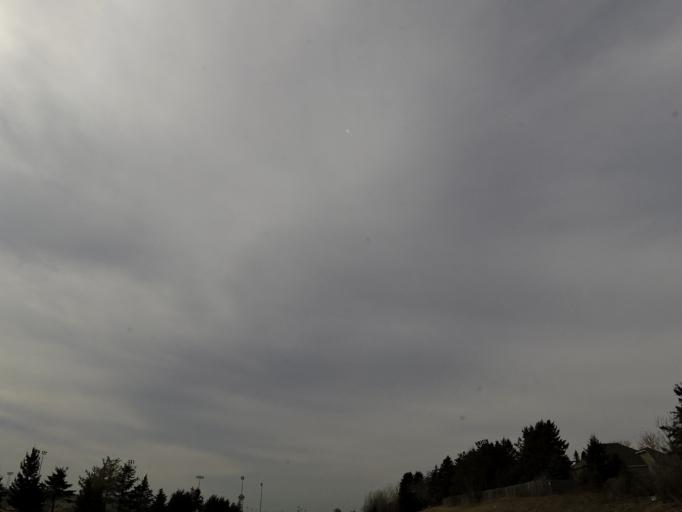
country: US
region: Minnesota
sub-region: Washington County
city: Woodbury
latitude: 44.8909
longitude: -92.9314
